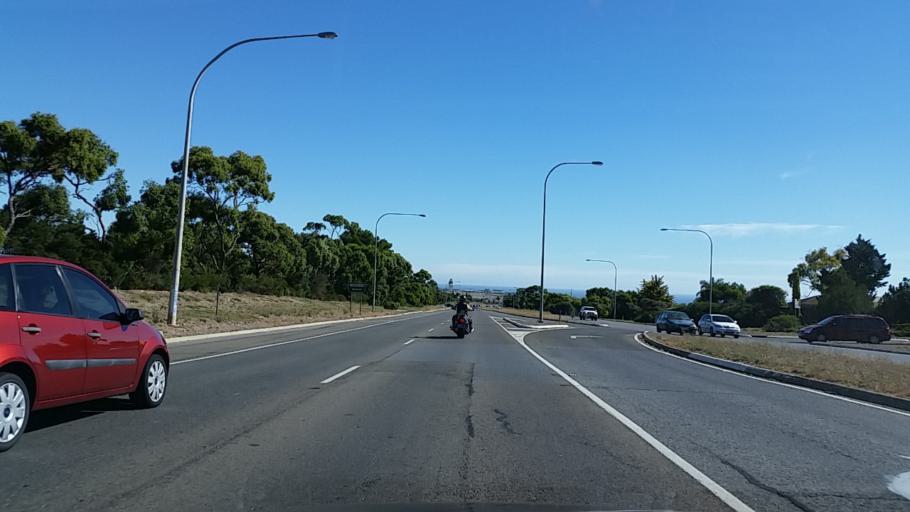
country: AU
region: South Australia
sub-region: Marion
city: Happy Valley
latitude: -35.0695
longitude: 138.5283
